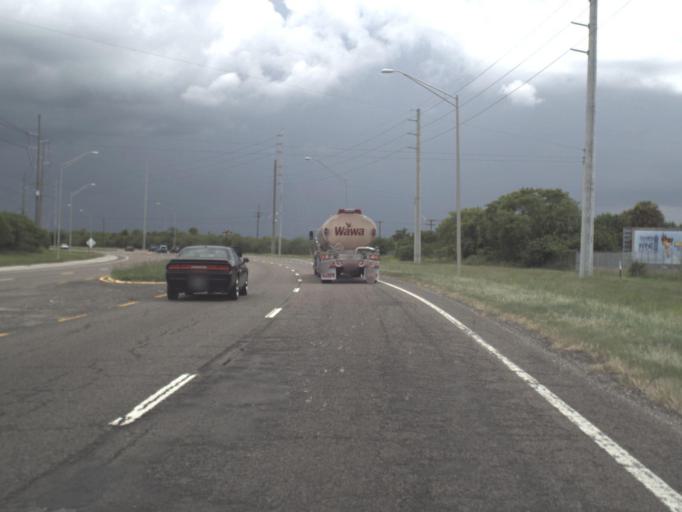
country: US
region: Florida
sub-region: Hillsborough County
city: Palm River-Clair Mel
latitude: 27.9242
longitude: -82.4197
